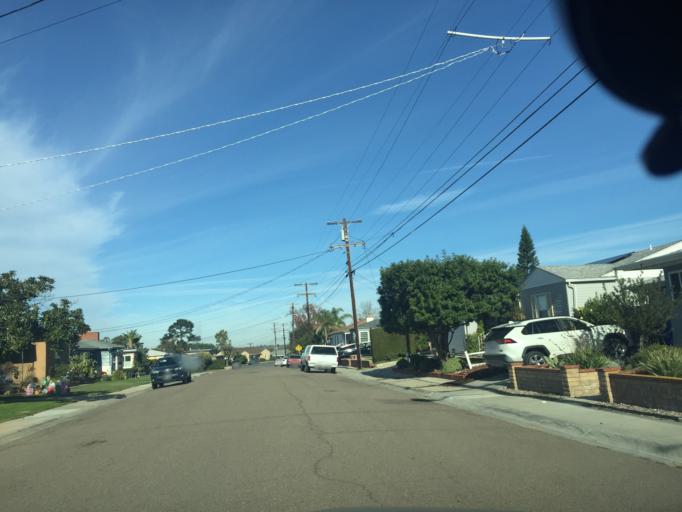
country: US
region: California
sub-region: San Diego County
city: Lemon Grove
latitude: 32.7650
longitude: -117.0811
